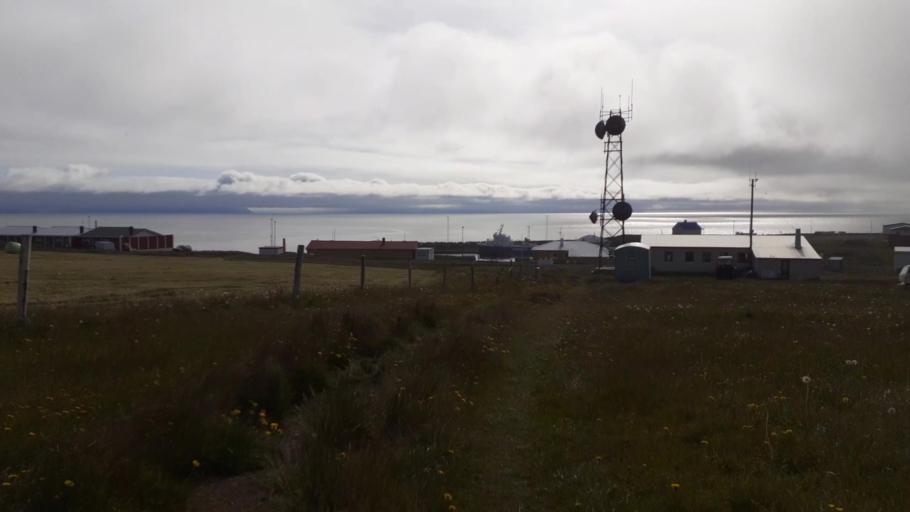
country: IS
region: Northeast
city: Dalvik
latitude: 66.5409
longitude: -18.0128
